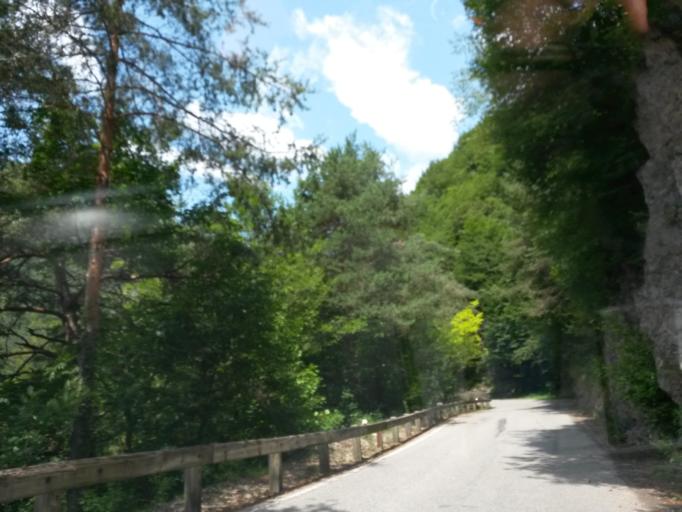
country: IT
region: Lombardy
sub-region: Provincia di Brescia
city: Gargnano
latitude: 45.7109
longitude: 10.6141
